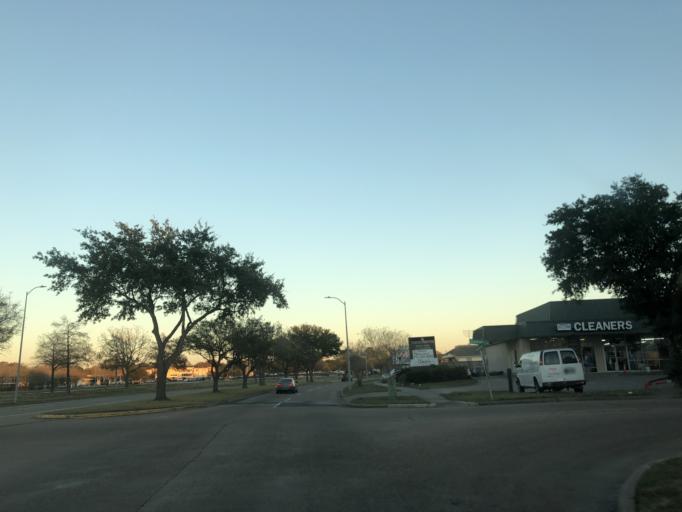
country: US
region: Texas
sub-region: Harris County
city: Bellaire
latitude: 29.6778
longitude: -95.4963
